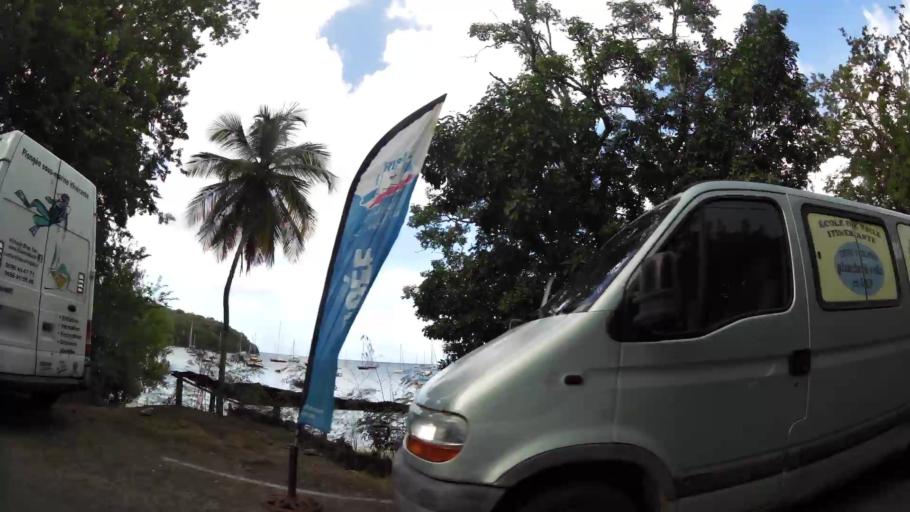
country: MQ
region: Martinique
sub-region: Martinique
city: Les Trois-Ilets
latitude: 14.5001
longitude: -61.0836
